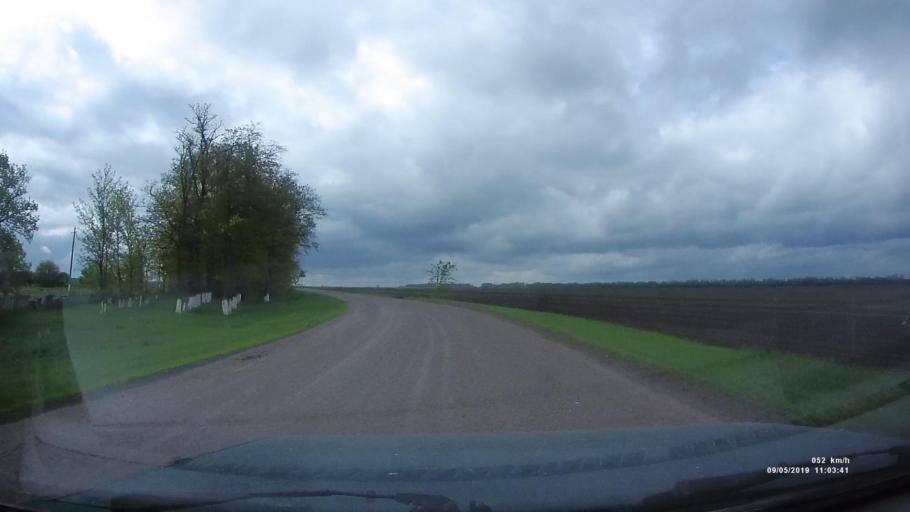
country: RU
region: Krasnodarskiy
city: Kanelovskaya
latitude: 46.8254
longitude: 39.2102
